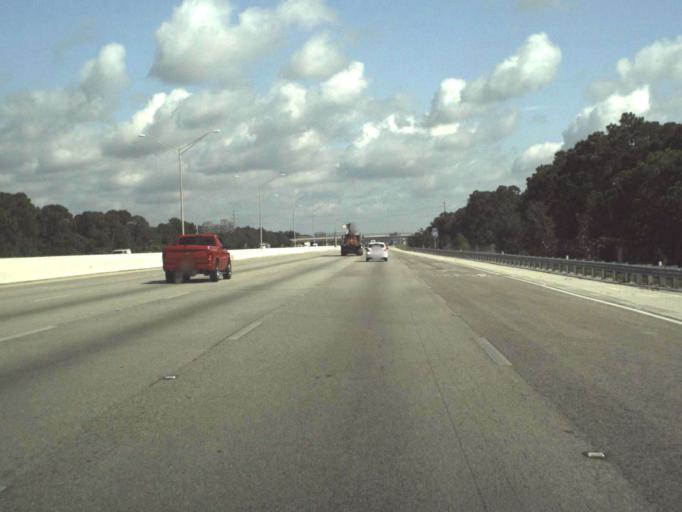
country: US
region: Florida
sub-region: Palm Beach County
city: Palm Beach Gardens
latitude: 26.8521
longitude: -80.1097
